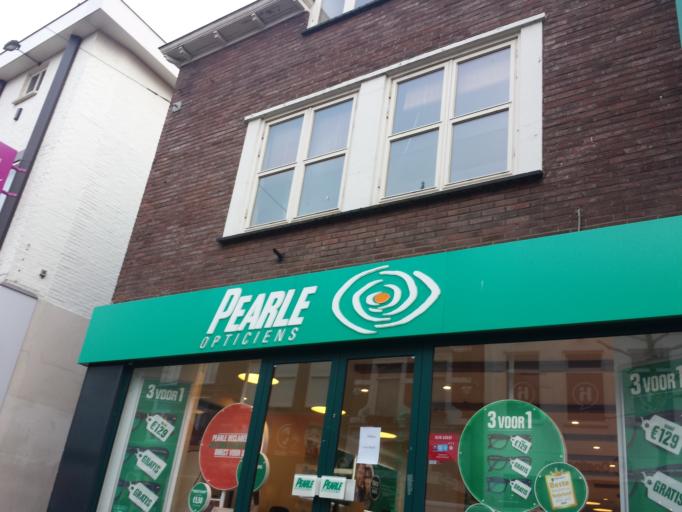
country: NL
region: Gelderland
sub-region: Gemeente Doetinchem
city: Doetinchem
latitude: 51.9652
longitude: 6.2895
